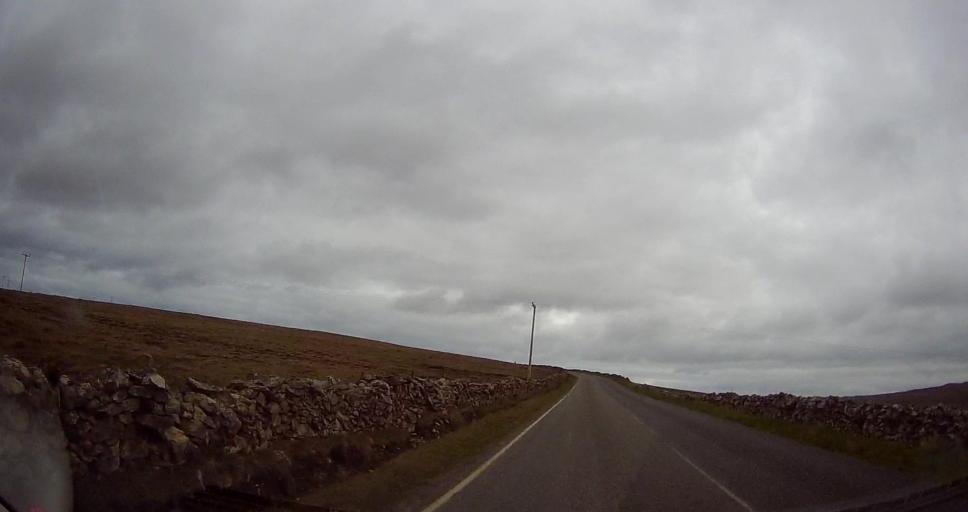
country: GB
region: Scotland
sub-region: Shetland Islands
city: Shetland
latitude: 60.7538
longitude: -0.8845
